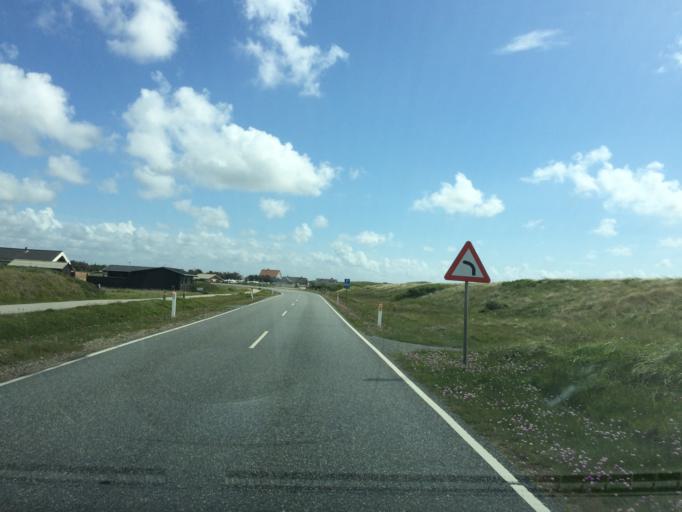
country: DK
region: Central Jutland
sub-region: Holstebro Kommune
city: Ulfborg
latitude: 56.3255
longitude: 8.1234
